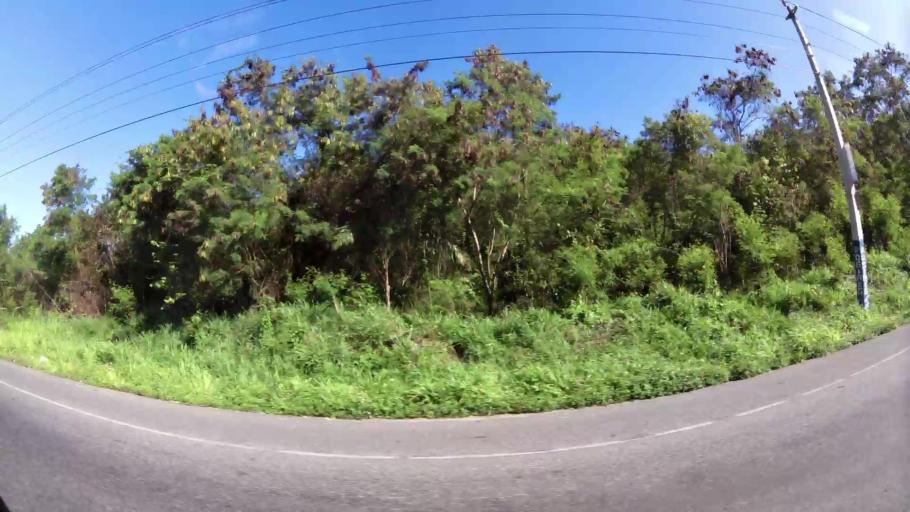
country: DO
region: San Cristobal
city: San Cristobal
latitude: 18.4322
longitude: -70.0912
